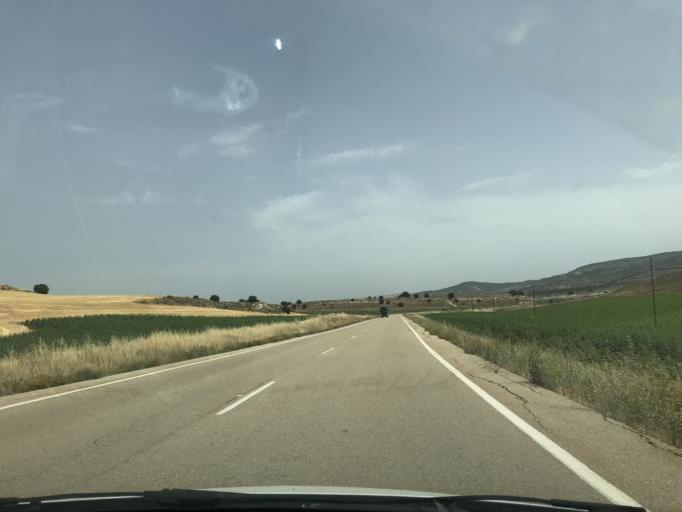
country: ES
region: Castille-La Mancha
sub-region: Provincia de Cuenca
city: Villar de Domingo Garcia
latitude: 40.2706
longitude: -2.3007
